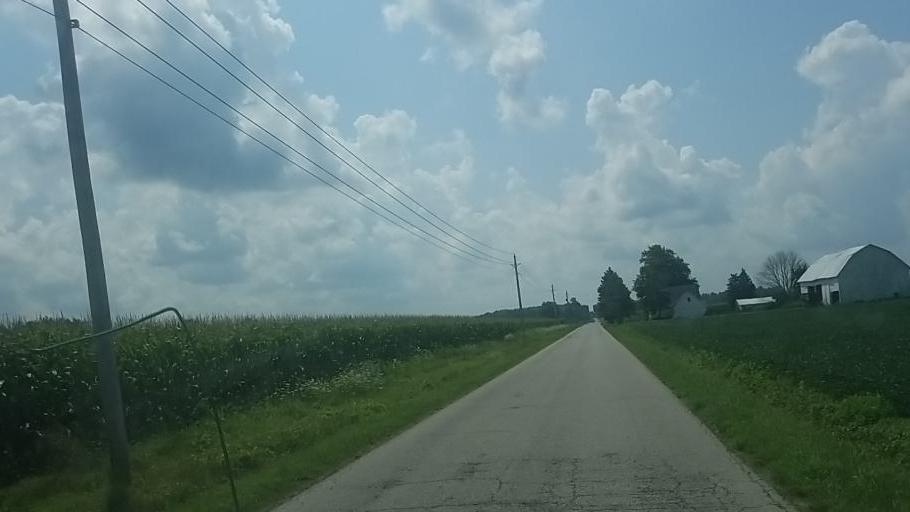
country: US
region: Ohio
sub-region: Crawford County
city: Galion
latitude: 40.8045
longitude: -82.8190
